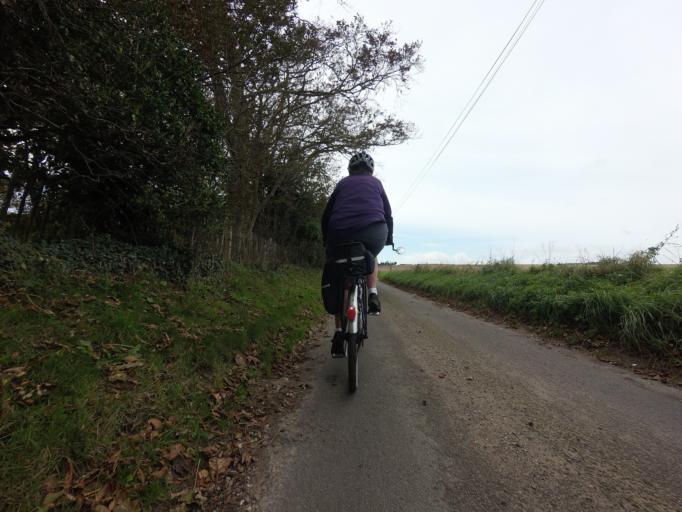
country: GB
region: England
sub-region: Norfolk
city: Wells-next-the-Sea
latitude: 52.9425
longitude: 0.7132
